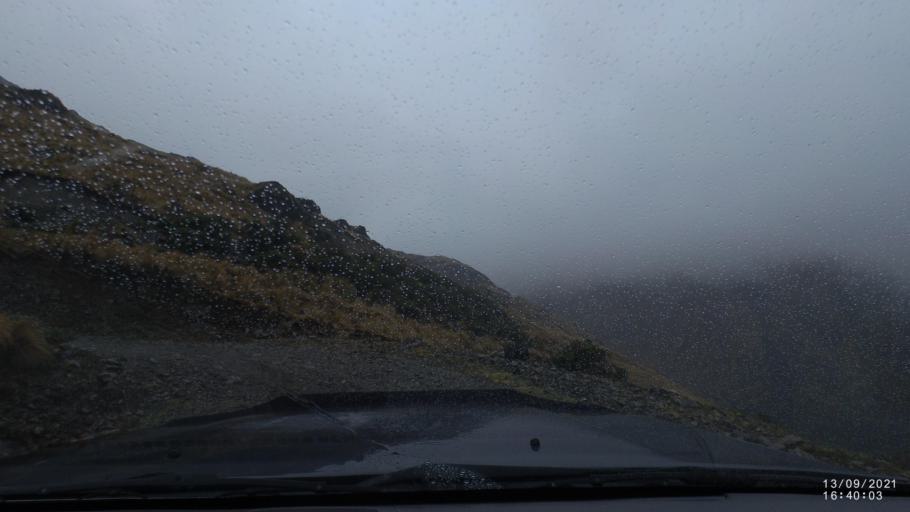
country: BO
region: Cochabamba
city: Colomi
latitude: -17.2809
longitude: -65.7097
